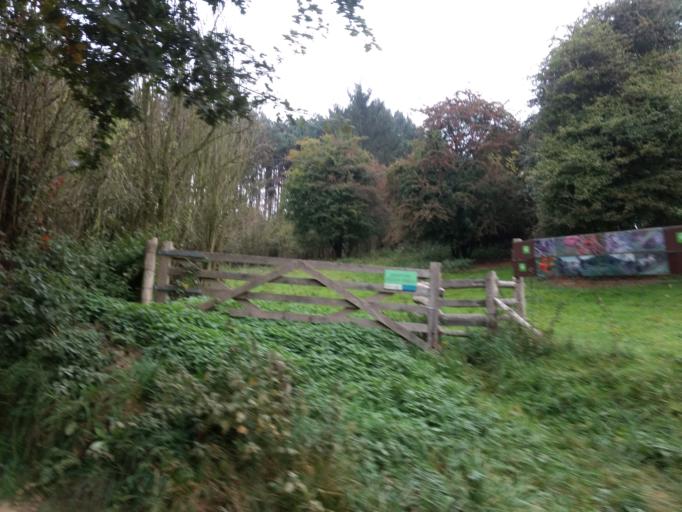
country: BE
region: Flanders
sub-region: Provincie Vlaams-Brabant
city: Bertem
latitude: 50.8717
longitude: 4.6423
